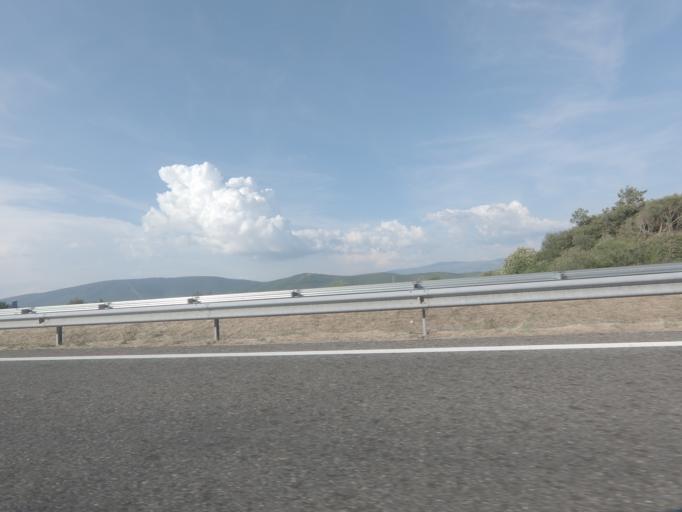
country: ES
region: Galicia
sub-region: Provincia de Ourense
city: Verin
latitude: 41.9606
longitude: -7.5152
